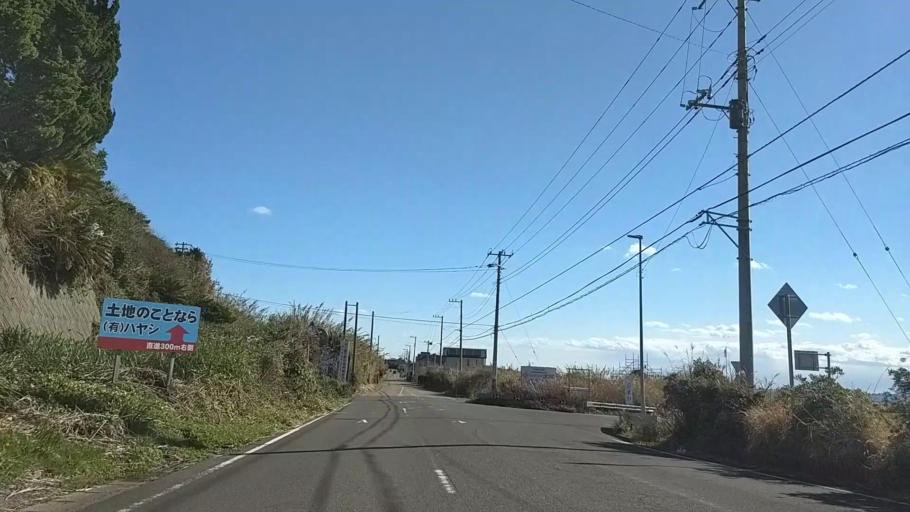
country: JP
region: Chiba
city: Tateyama
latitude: 34.9086
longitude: 139.8315
